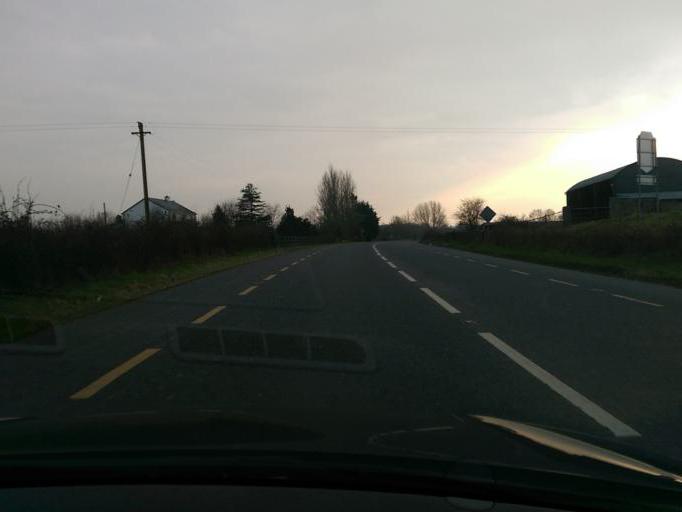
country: IE
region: Leinster
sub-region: An Longfort
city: Ballymahon
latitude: 53.5097
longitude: -7.8271
